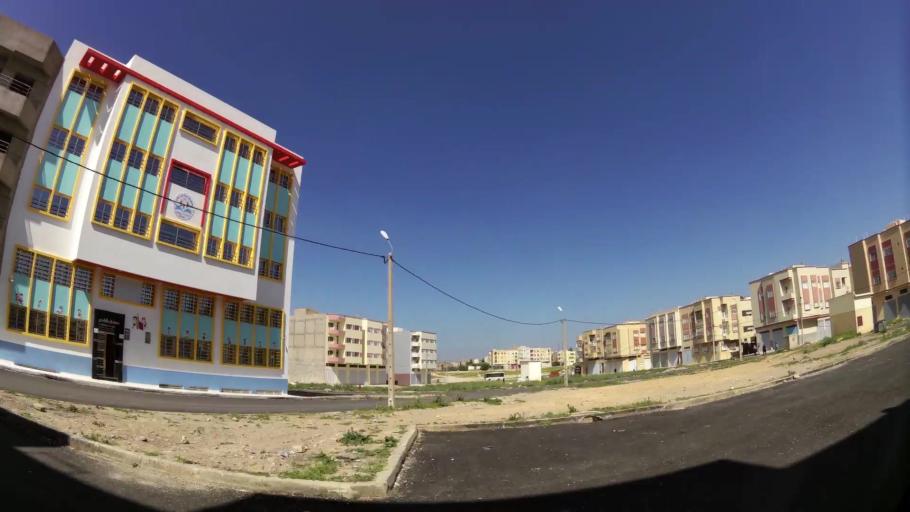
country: MA
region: Fes-Boulemane
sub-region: Fes
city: Fes
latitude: 34.0114
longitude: -5.0361
